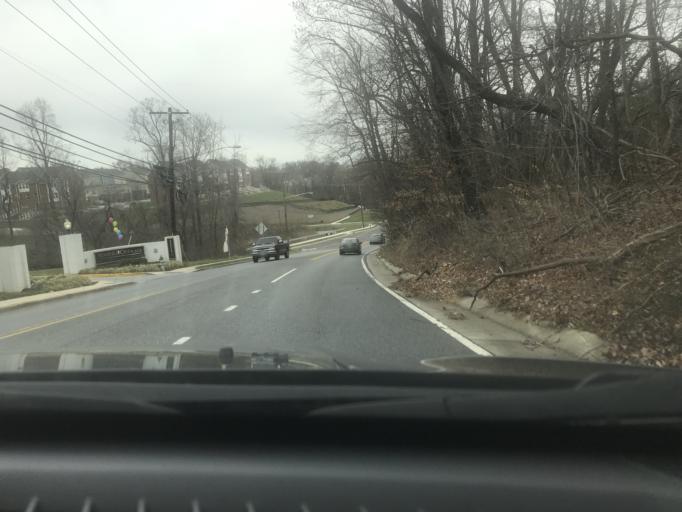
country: US
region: Maryland
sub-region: Prince George's County
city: Temple Hills
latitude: 38.8058
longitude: -76.9630
